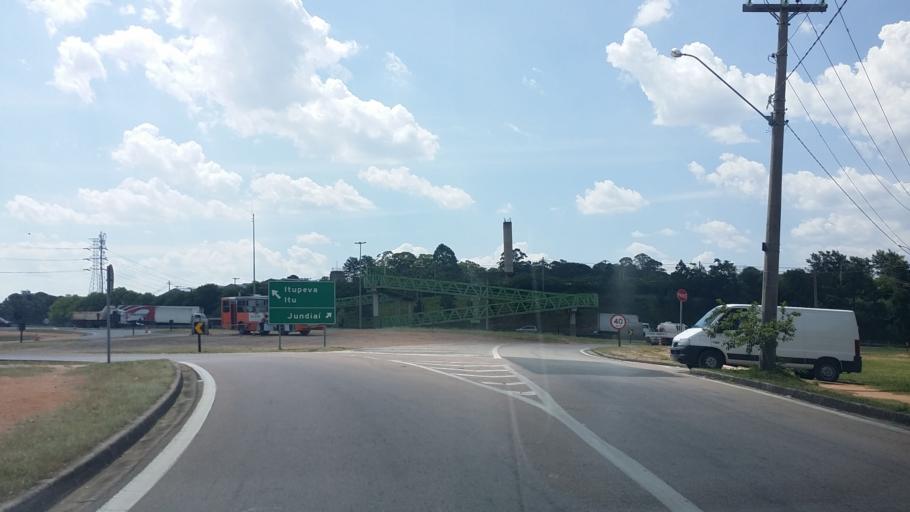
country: BR
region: Sao Paulo
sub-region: Jundiai
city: Jundiai
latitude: -23.1841
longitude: -46.9676
